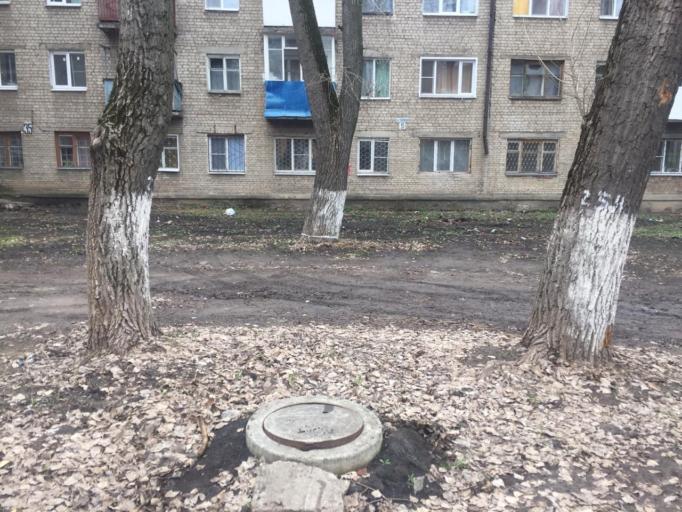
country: RU
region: Voronezj
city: Voronezh
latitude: 51.6787
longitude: 39.1540
